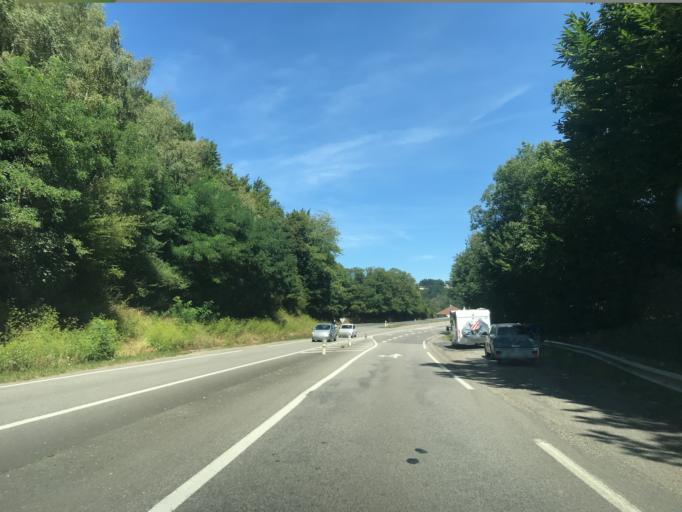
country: FR
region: Limousin
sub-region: Departement de la Correze
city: Naves
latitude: 45.2937
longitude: 1.8076
